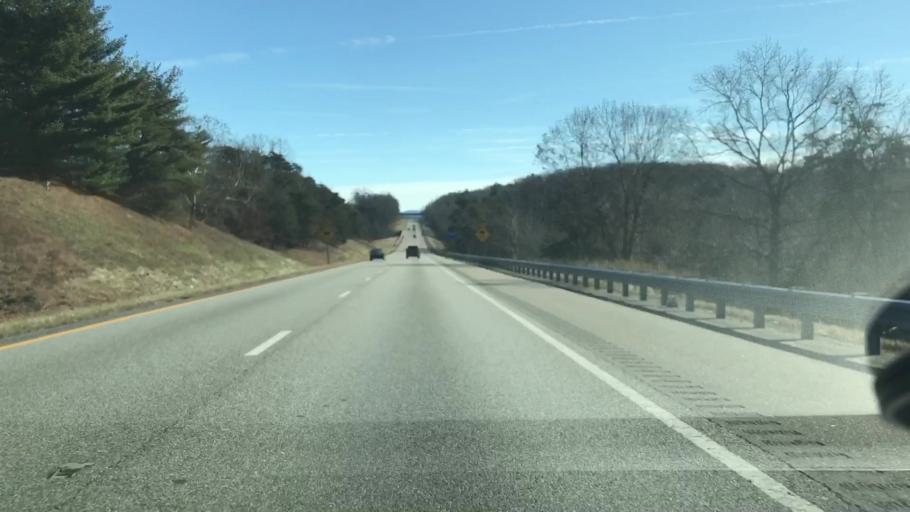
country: US
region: Virginia
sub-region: Augusta County
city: Jolivue
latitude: 38.1105
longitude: -79.0240
